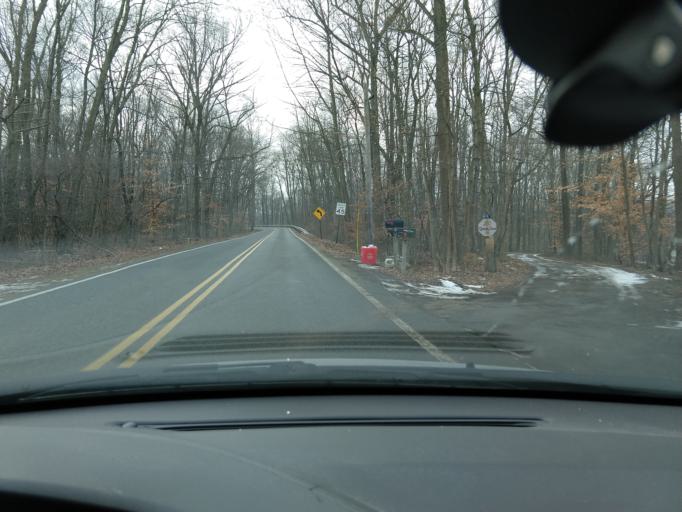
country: US
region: Pennsylvania
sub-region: Berks County
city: Birdsboro
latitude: 40.2429
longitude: -75.7746
